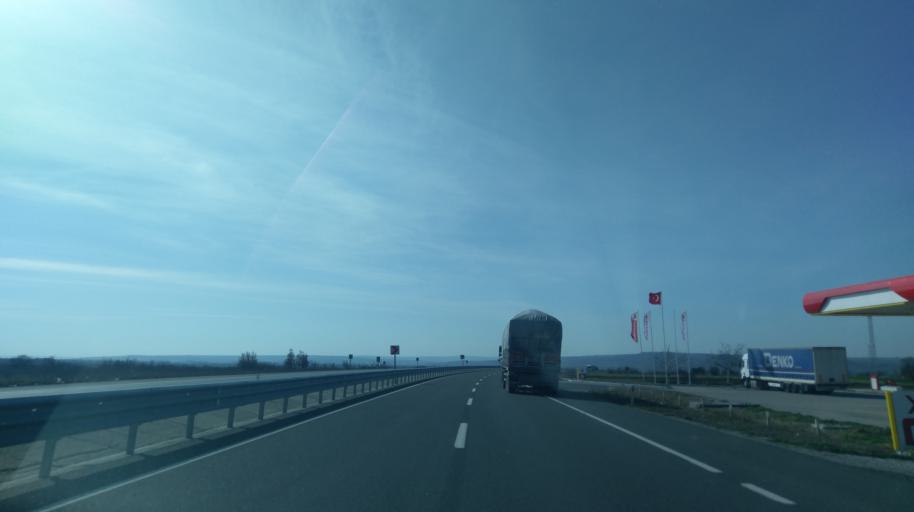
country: TR
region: Edirne
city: Hamidiye
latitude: 41.1330
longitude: 26.6592
